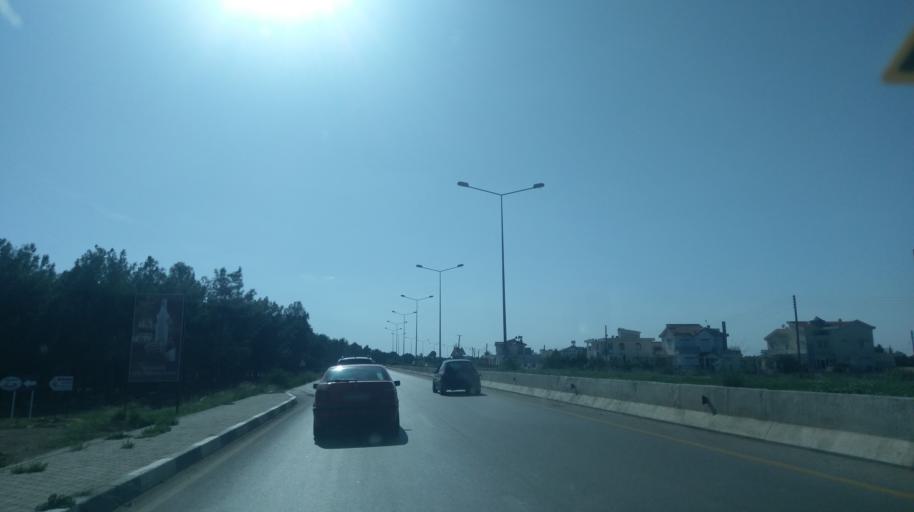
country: CY
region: Ammochostos
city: Trikomo
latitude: 35.2043
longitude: 33.8946
